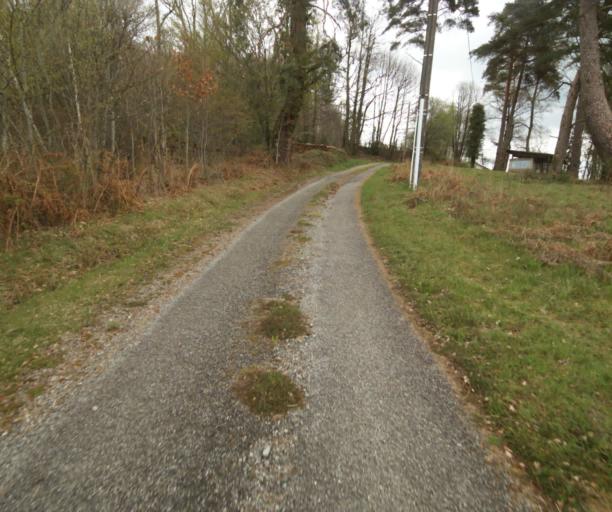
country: FR
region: Limousin
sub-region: Departement de la Correze
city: Laguenne
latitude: 45.2467
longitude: 1.8705
